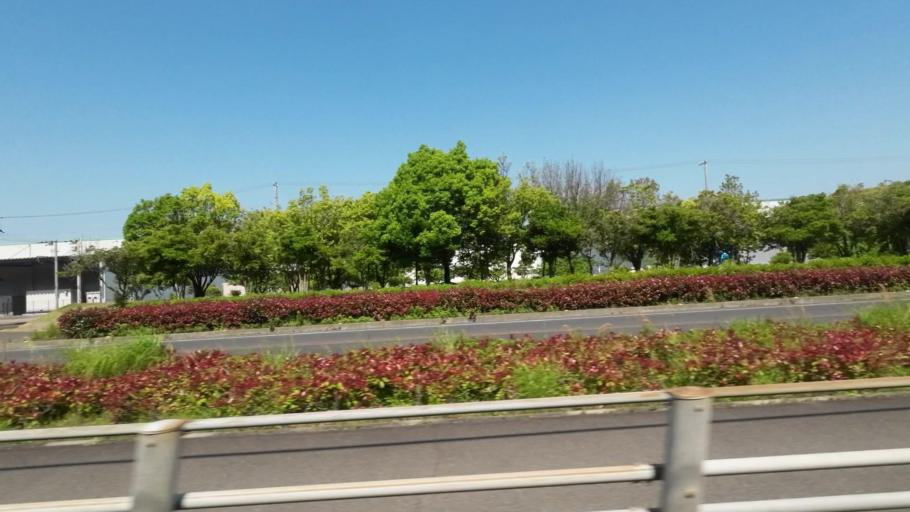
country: JP
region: Ehime
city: Kawanoecho
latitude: 34.0260
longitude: 133.5817
